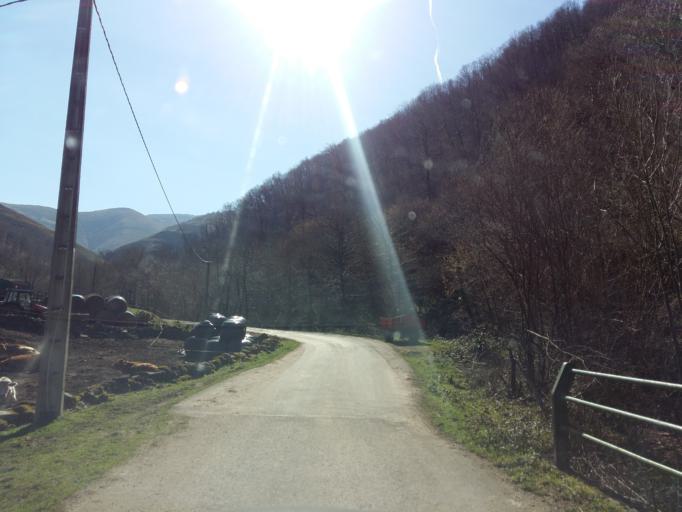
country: ES
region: Cantabria
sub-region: Provincia de Cantabria
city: Vega de Pas
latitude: 43.1378
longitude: -3.7927
